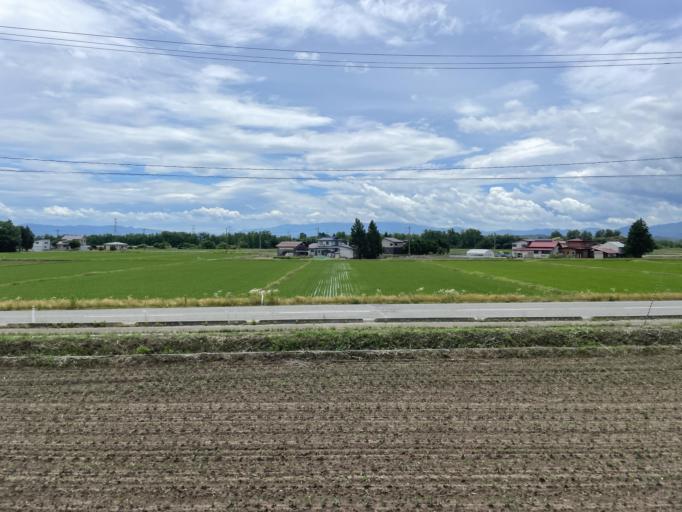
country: JP
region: Yamagata
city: Nagai
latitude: 38.0690
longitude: 140.0246
